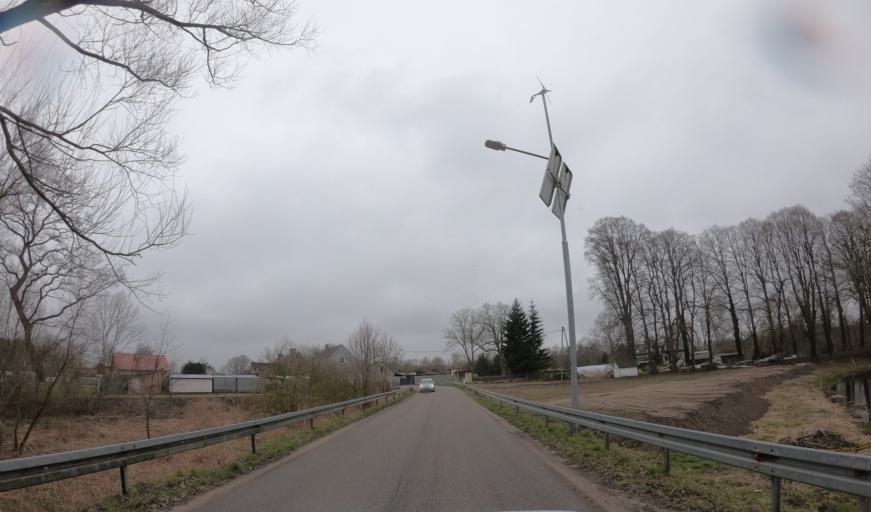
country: PL
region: West Pomeranian Voivodeship
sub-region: Powiat kamienski
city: Kamien Pomorski
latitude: 53.9206
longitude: 14.8669
